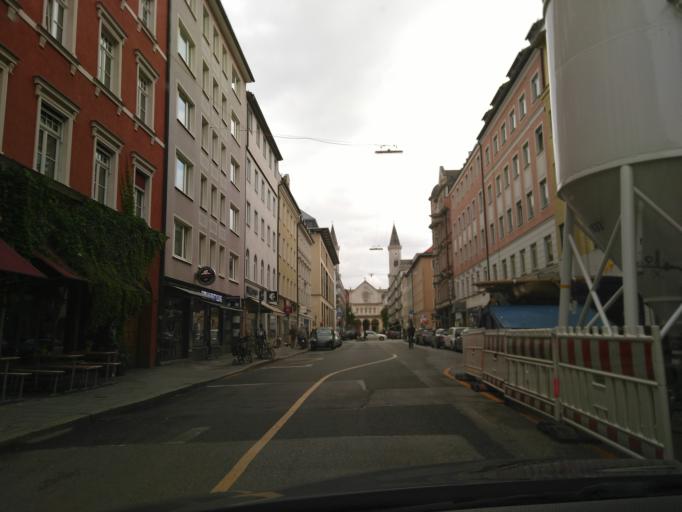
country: DE
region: Bavaria
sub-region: Upper Bavaria
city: Munich
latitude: 48.1500
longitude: 11.5771
